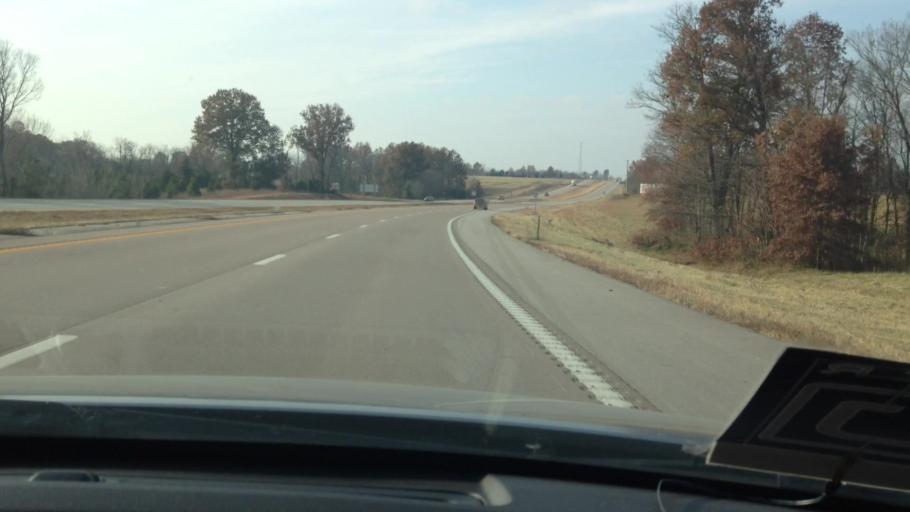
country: US
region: Missouri
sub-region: Cass County
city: Garden City
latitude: 38.4689
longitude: -94.0094
